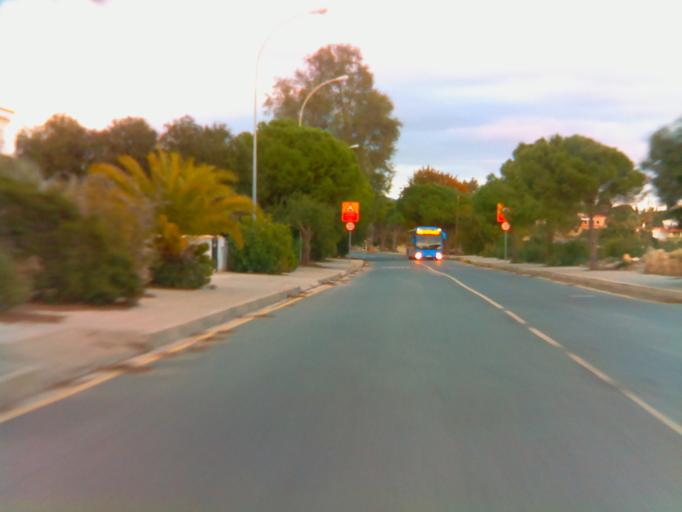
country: CY
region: Pafos
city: Pegeia
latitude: 34.8560
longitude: 32.3684
